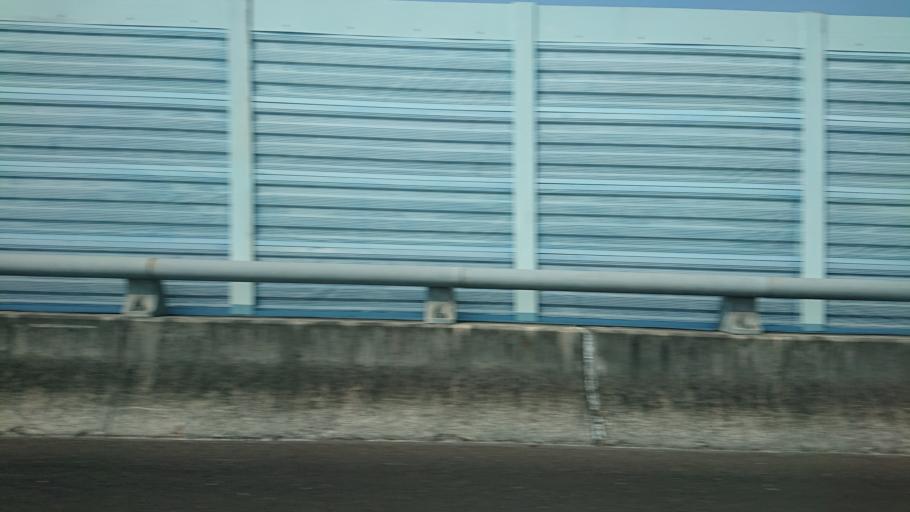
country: TW
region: Taiwan
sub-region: Nantou
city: Nantou
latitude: 23.8932
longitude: 120.7109
